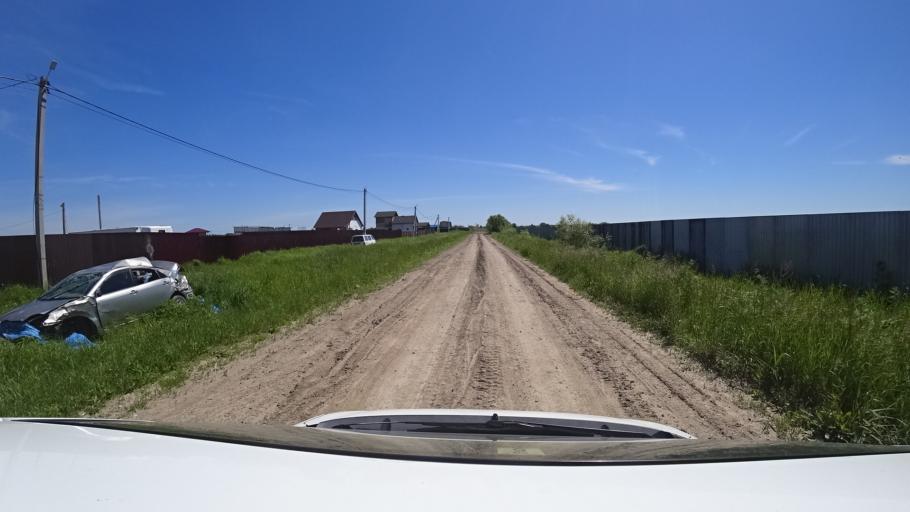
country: RU
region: Khabarovsk Krai
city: Topolevo
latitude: 48.5098
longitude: 135.2022
